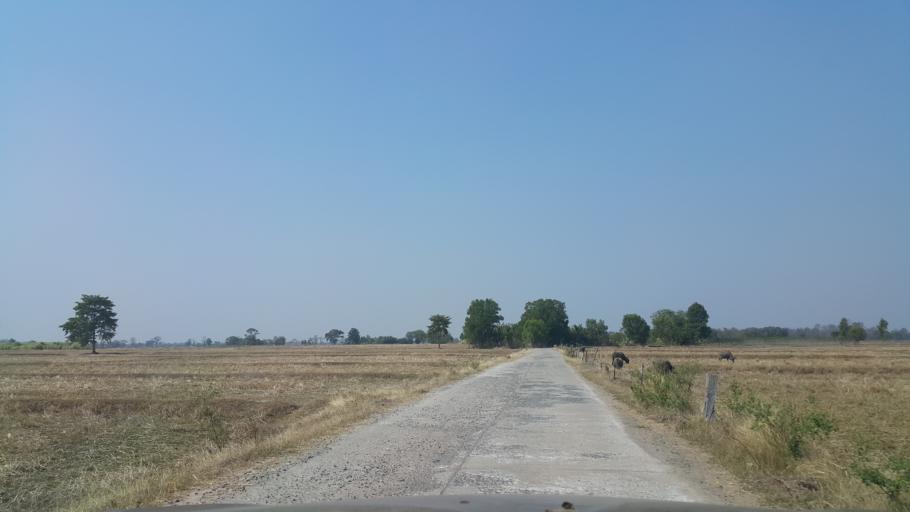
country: TH
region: Buriram
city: Krasang
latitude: 15.0906
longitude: 103.3836
